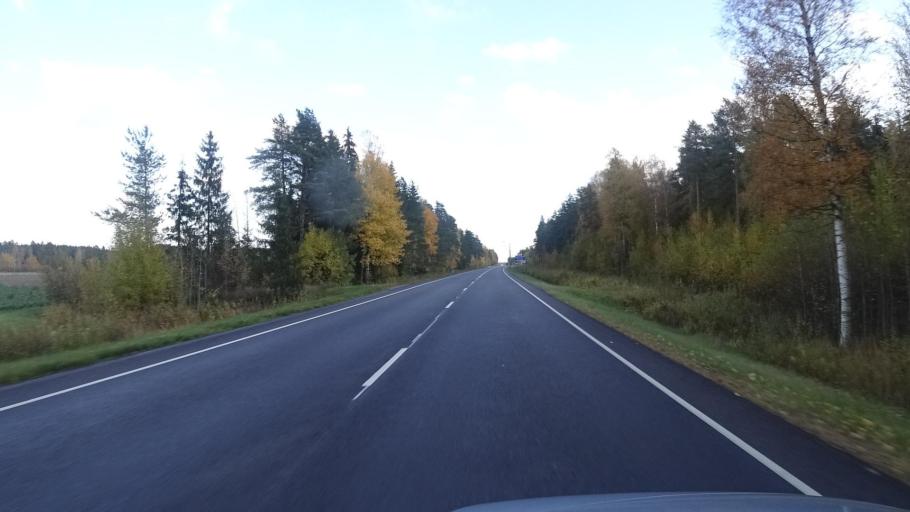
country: FI
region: Satakunta
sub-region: Rauma
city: Koeylioe
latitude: 61.0837
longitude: 22.2671
